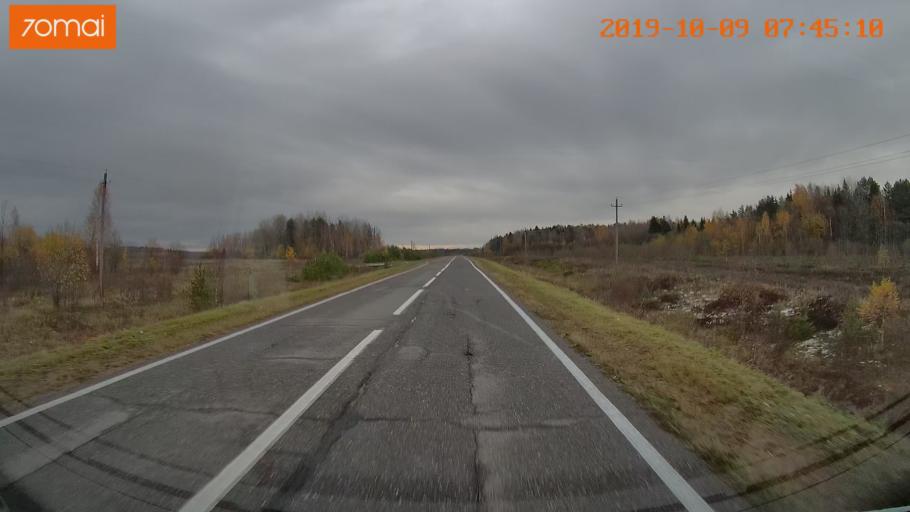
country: RU
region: Jaroslavl
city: Kukoboy
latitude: 58.6522
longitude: 39.7620
